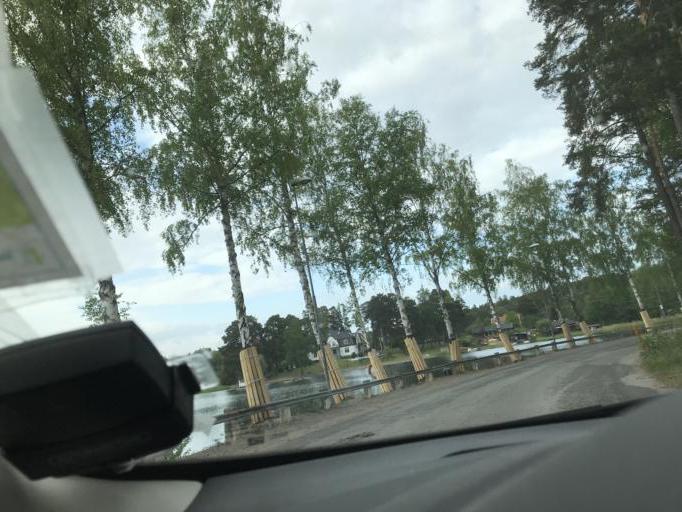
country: SE
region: Stockholm
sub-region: Botkyrka Kommun
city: Varsta
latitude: 59.1931
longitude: 17.8003
